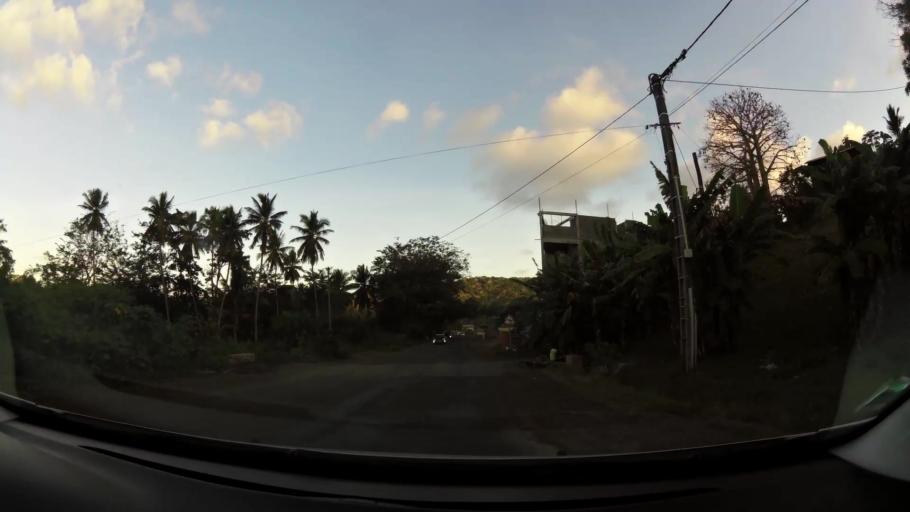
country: YT
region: Dembeni
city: Dembeni
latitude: -12.8647
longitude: 45.1983
